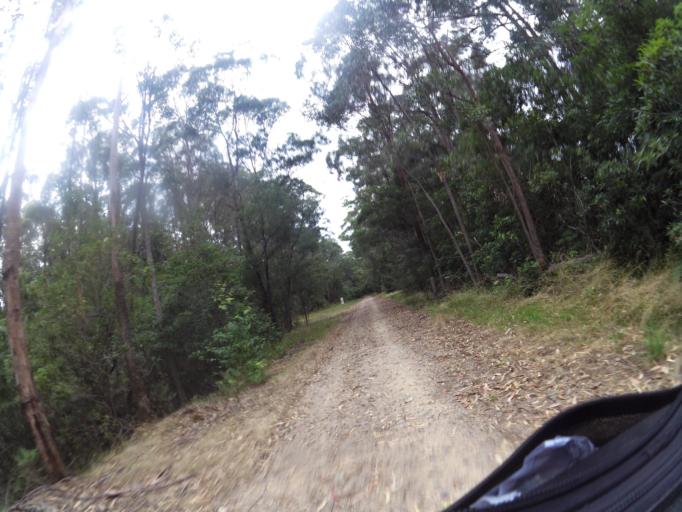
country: AU
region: Victoria
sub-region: East Gippsland
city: Lakes Entrance
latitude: -37.7356
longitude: 148.4240
